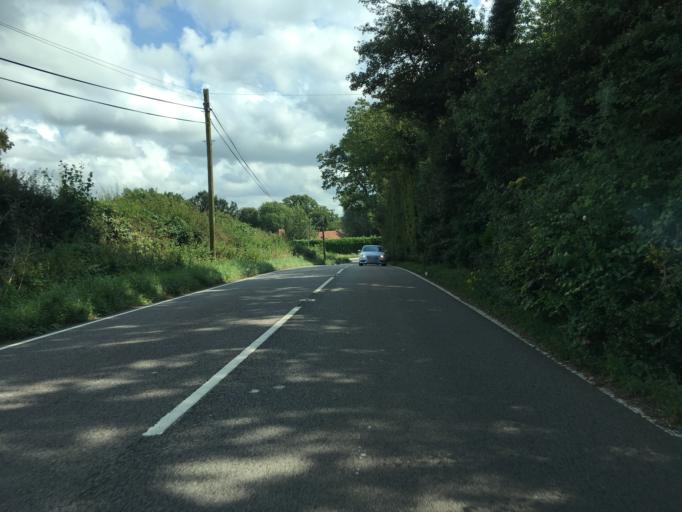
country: GB
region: England
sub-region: Kent
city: Headcorn
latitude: 51.1328
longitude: 0.6443
